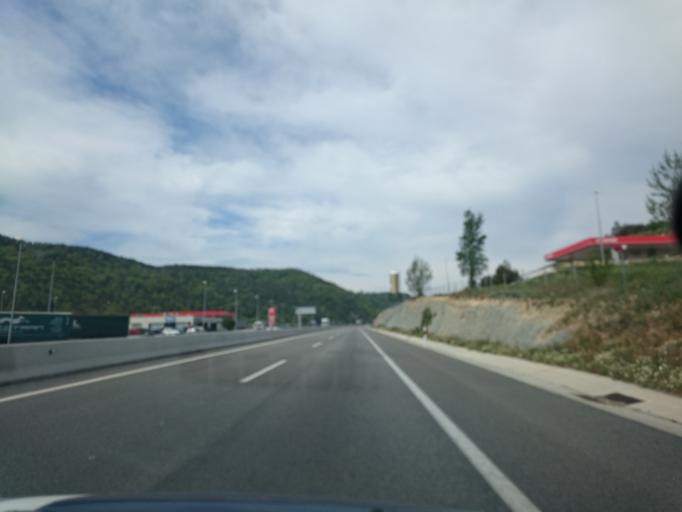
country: ES
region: Catalonia
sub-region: Provincia de Barcelona
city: Gurb
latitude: 41.9339
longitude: 2.1950
